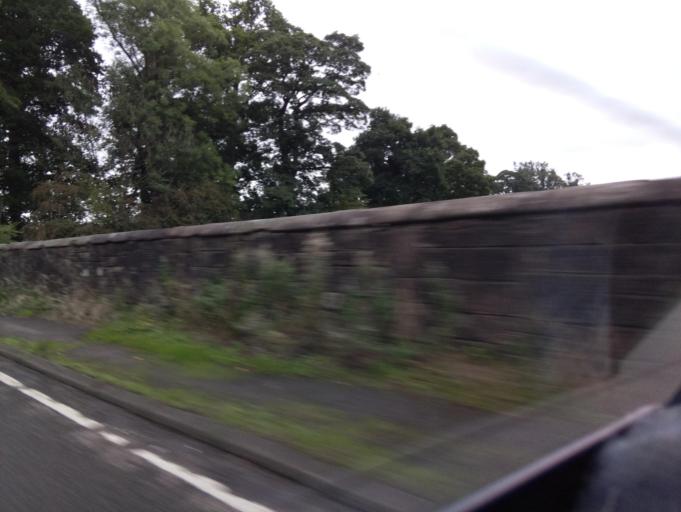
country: GB
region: Scotland
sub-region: Clackmannanshire
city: Tillicoultry
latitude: 56.1547
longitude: -3.7252
